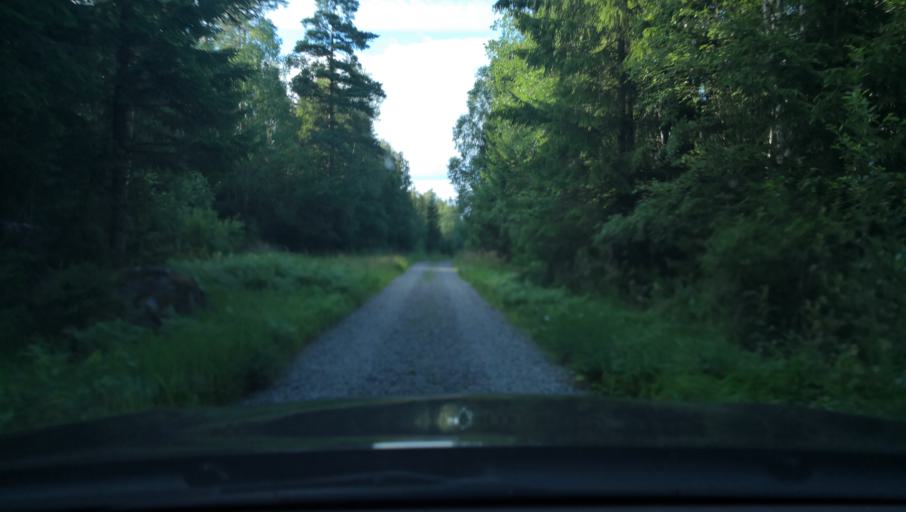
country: SE
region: Uppsala
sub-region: Osthammars Kommun
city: Osterbybruk
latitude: 60.0280
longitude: 17.9177
